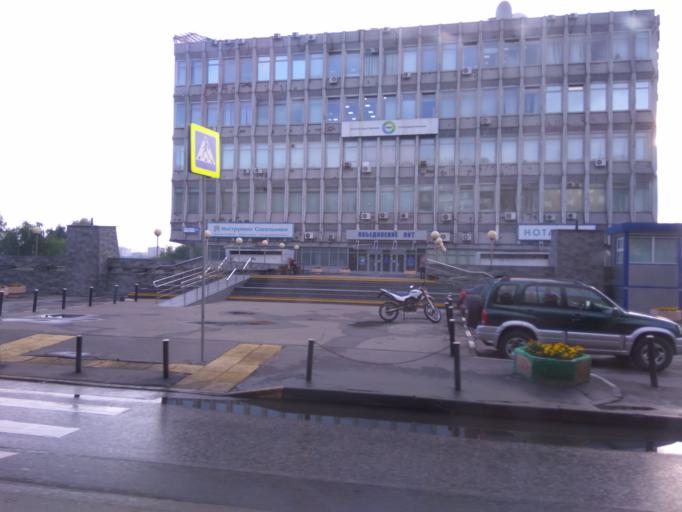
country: RU
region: Moskovskaya
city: Bogorodskoye
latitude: 55.8066
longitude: 37.7066
